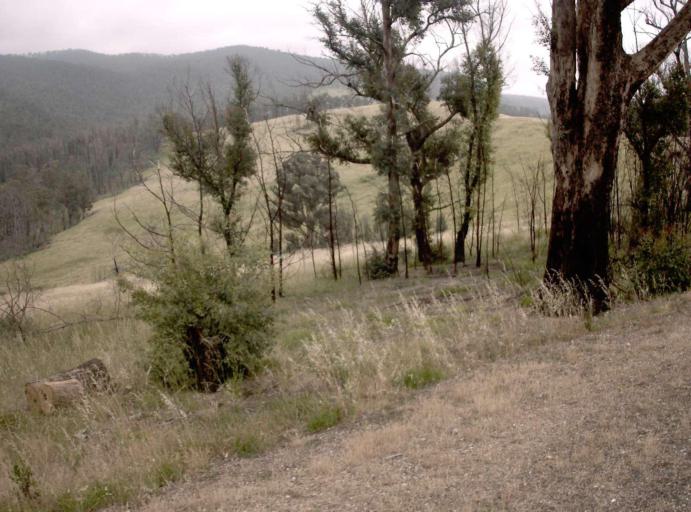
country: AU
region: Victoria
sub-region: Wellington
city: Heyfield
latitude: -37.8291
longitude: 146.6775
